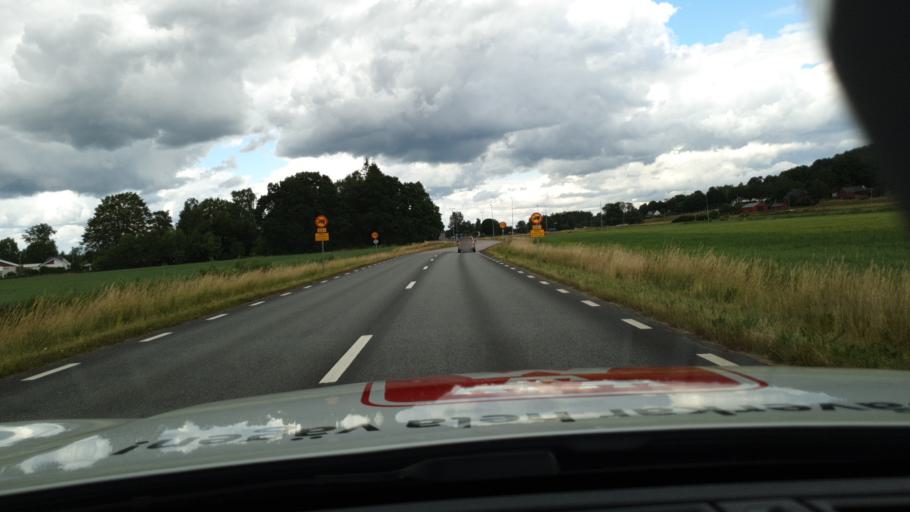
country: SE
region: Skane
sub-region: Hassleholms Kommun
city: Tormestorp
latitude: 56.1165
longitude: 13.7330
